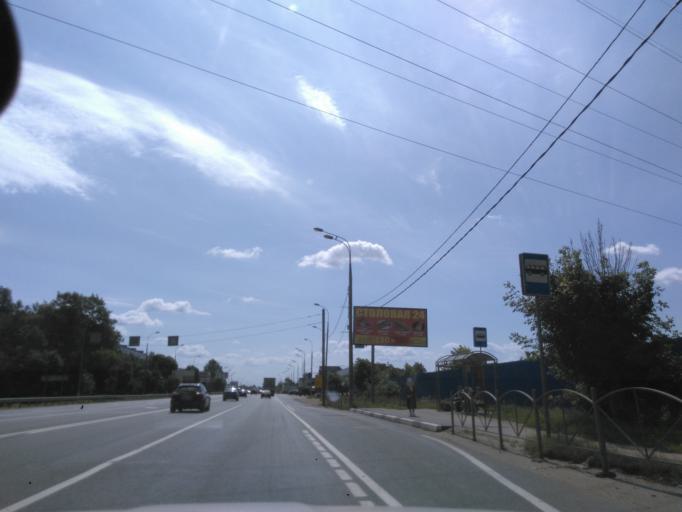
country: RU
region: Moskovskaya
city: Solnechnogorsk
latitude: 56.1789
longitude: 36.9912
